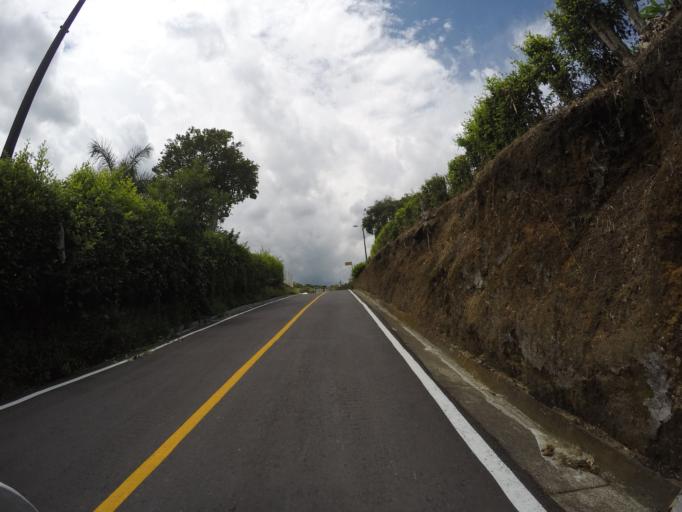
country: CO
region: Quindio
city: Quimbaya
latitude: 4.6123
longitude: -75.7583
